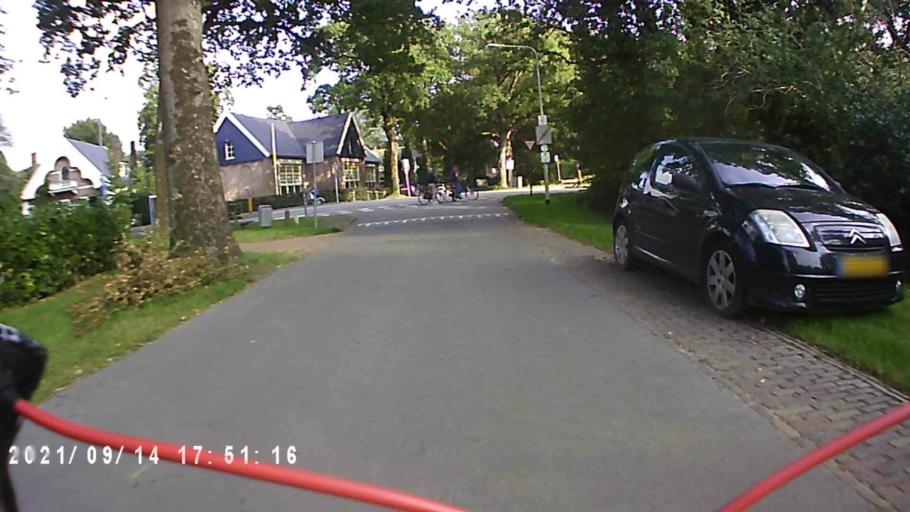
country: NL
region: Groningen
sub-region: Gemeente Haren
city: Haren
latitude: 53.1355
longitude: 6.6283
